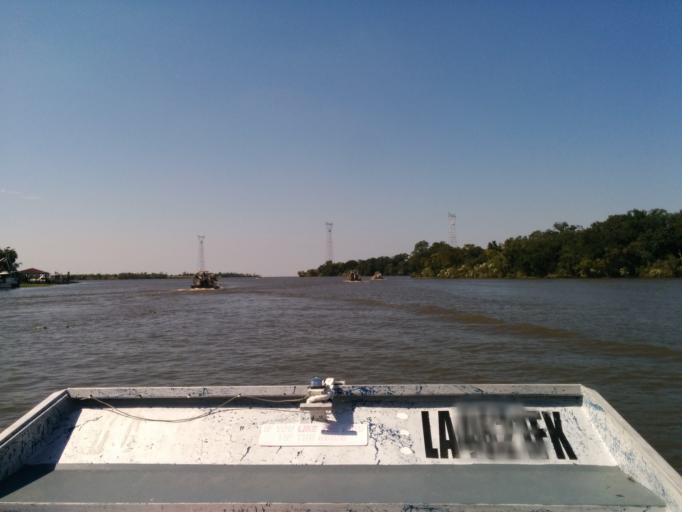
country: US
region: Louisiana
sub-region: Jefferson Parish
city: Jean Lafitte
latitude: 29.7421
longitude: -90.1342
